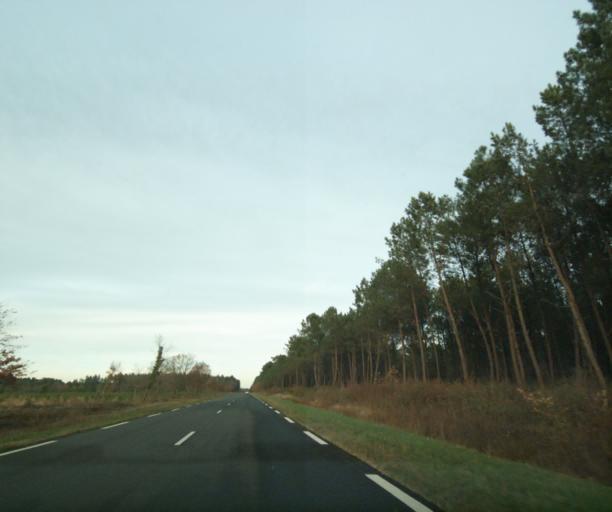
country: FR
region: Aquitaine
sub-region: Departement de la Gironde
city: Bazas
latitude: 44.3270
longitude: -0.2400
